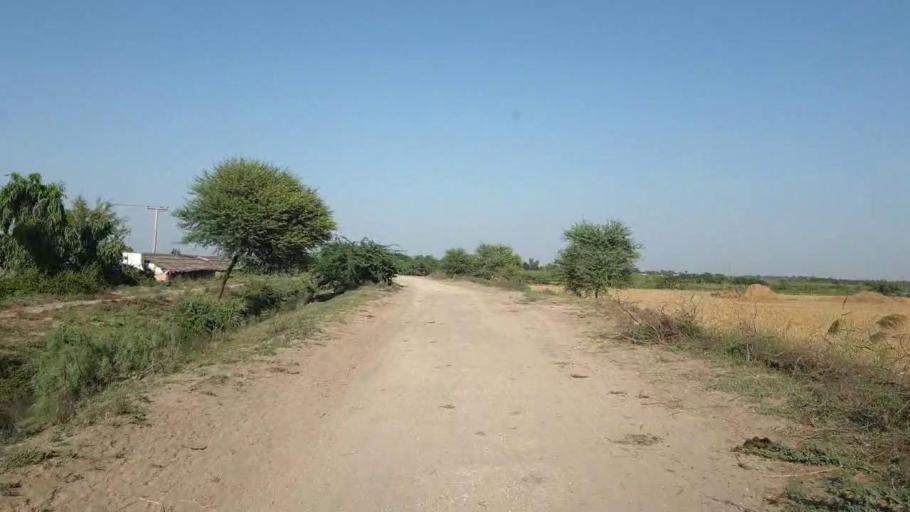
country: PK
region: Sindh
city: Badin
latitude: 24.6062
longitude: 68.9253
